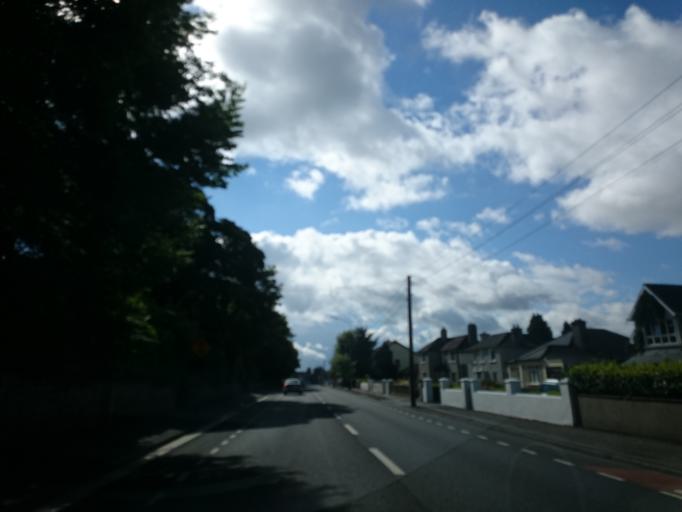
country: IE
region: Leinster
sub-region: Kilkenny
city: Kilkenny
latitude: 52.6629
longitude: -7.2507
